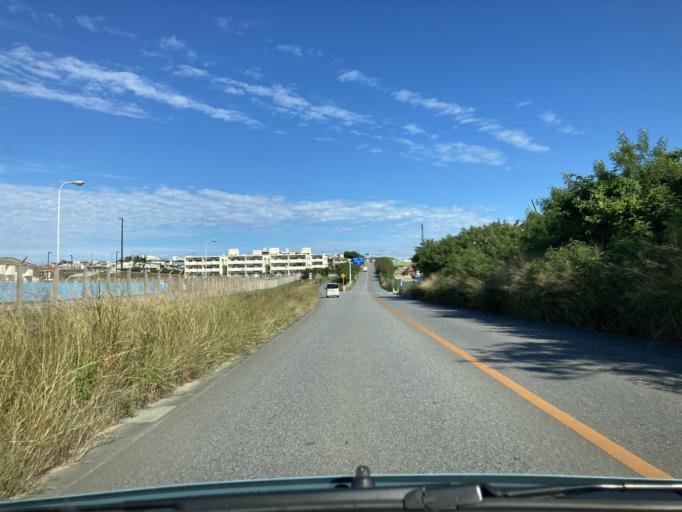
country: JP
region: Okinawa
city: Okinawa
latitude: 26.3777
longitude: 127.7455
